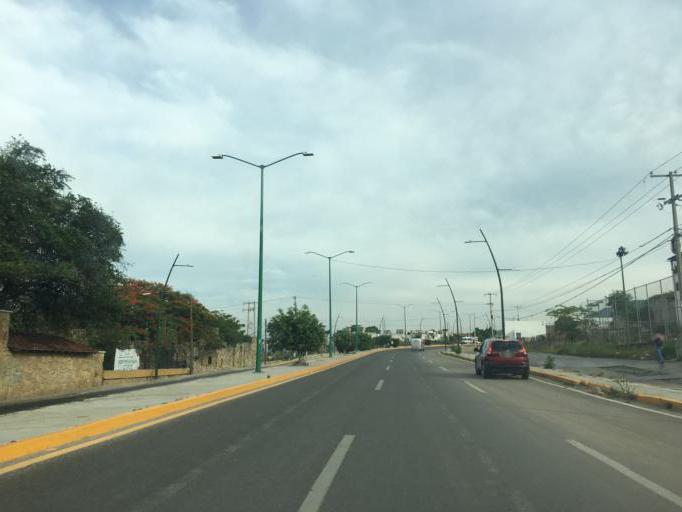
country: MX
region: Chiapas
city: Tuxtla Gutierrez
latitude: 16.7669
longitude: -93.1688
